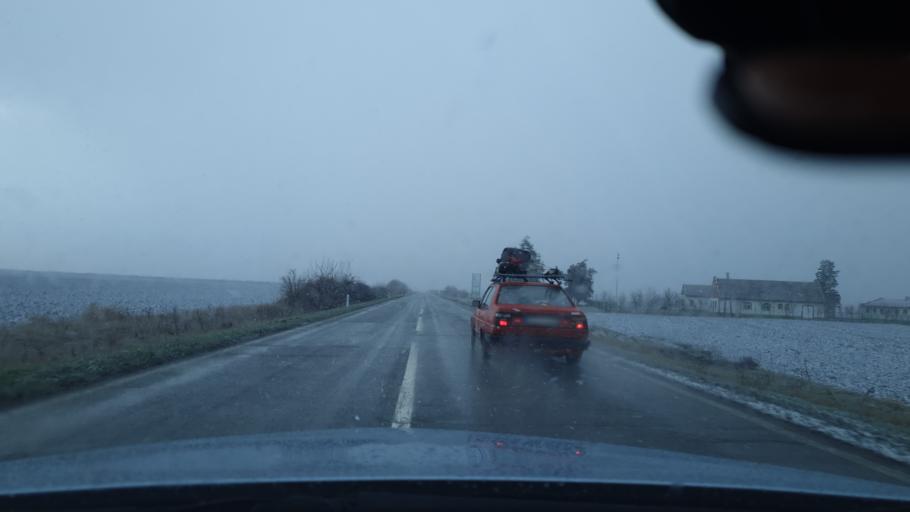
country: RS
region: Autonomna Pokrajina Vojvodina
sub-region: Juznobanatski Okrug
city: Pancevo
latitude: 44.8593
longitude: 20.7466
